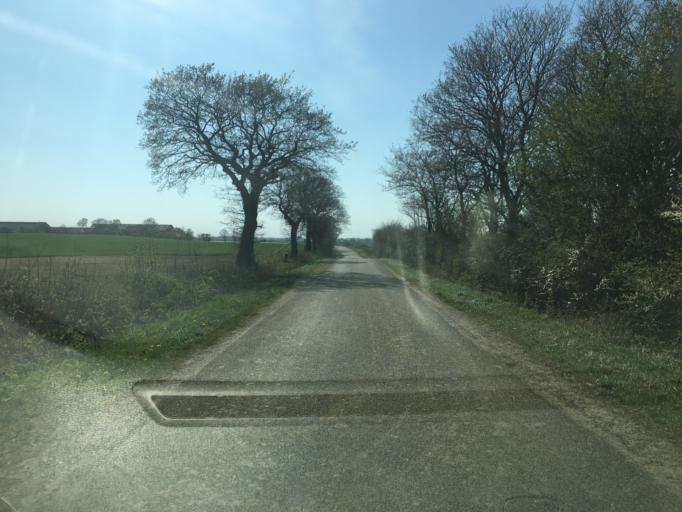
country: DK
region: South Denmark
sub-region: Aabenraa Kommune
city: Rodekro
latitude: 54.9987
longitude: 9.3256
